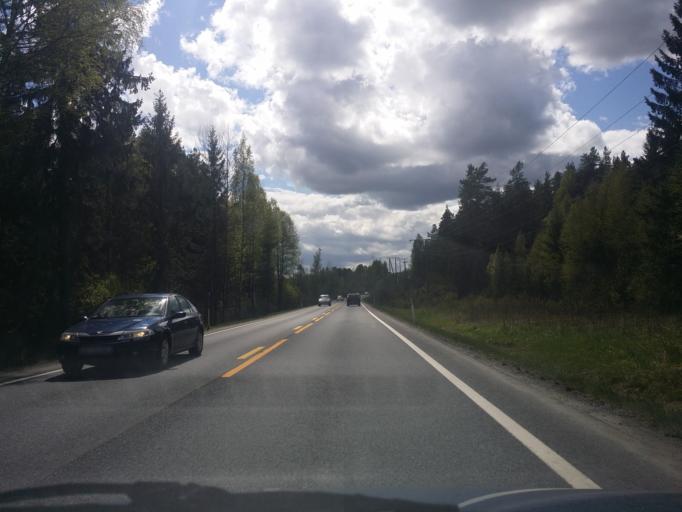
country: NO
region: Buskerud
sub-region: Modum
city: Vikersund
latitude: 59.9540
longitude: 9.9752
